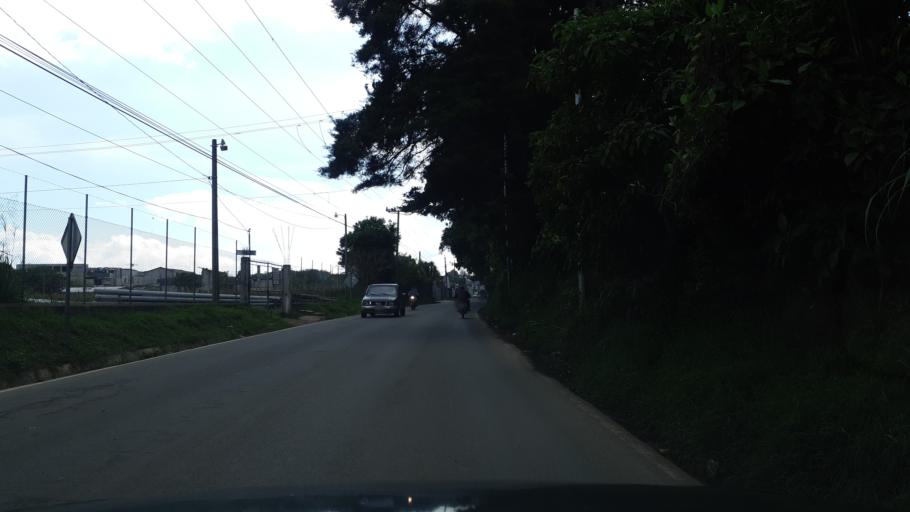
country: GT
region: Chimaltenango
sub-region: Municipio de Chimaltenango
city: Chimaltenango
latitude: 14.6684
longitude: -90.8077
